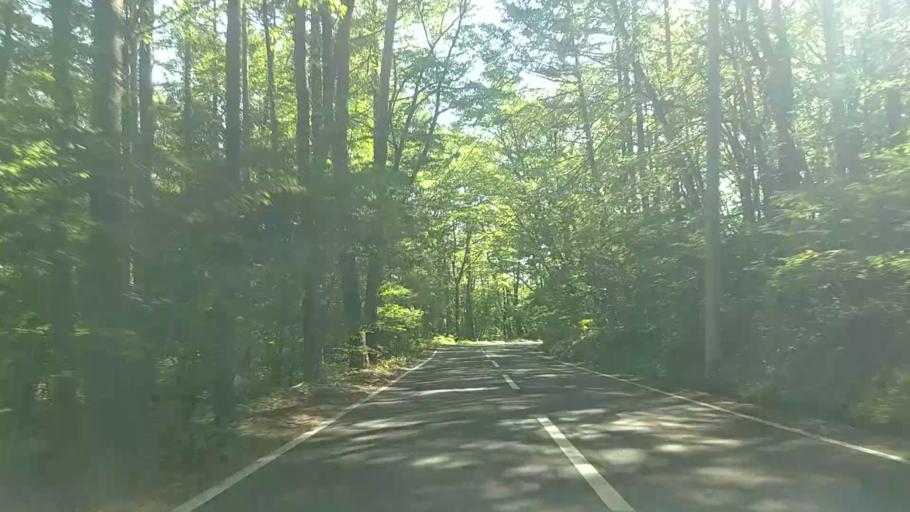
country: JP
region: Yamanashi
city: Nirasaki
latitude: 35.8854
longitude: 138.3817
